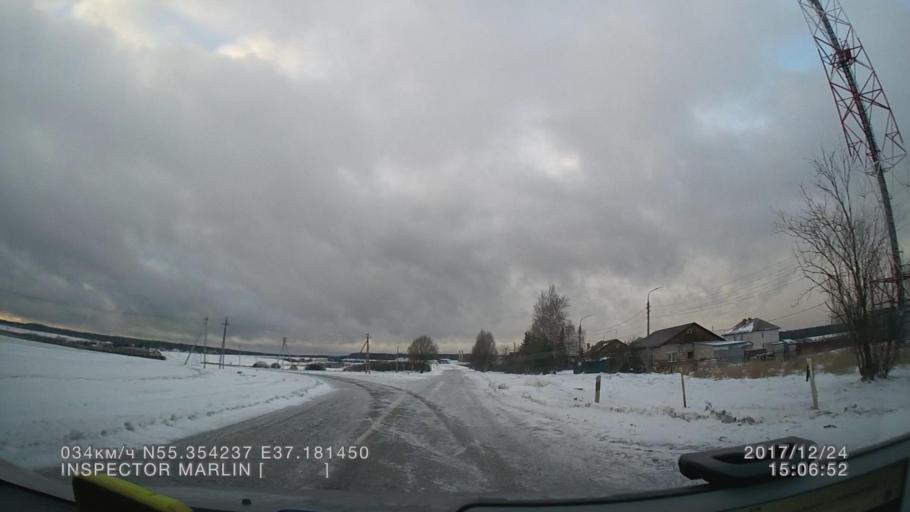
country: RU
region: Moskovskaya
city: Troitsk
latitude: 55.3543
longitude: 37.1814
